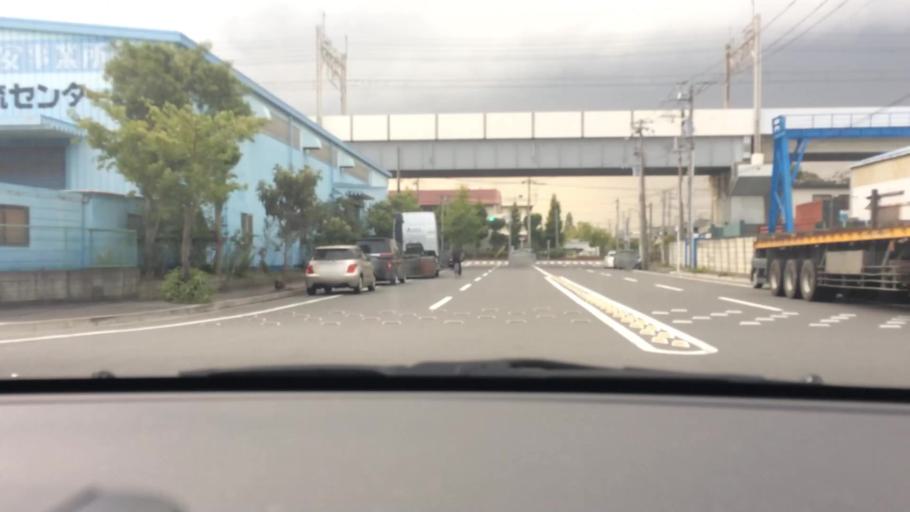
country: JP
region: Tokyo
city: Urayasu
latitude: 35.6368
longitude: 139.8990
